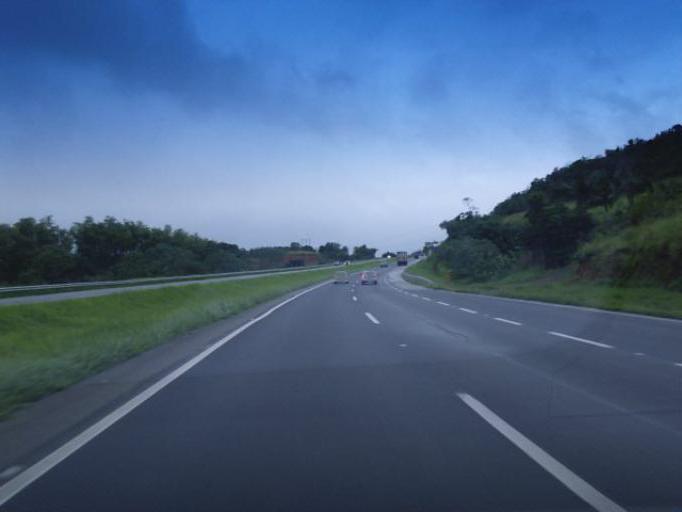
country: BR
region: Sao Paulo
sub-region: Miracatu
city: Miracatu
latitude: -24.2934
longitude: -47.4769
